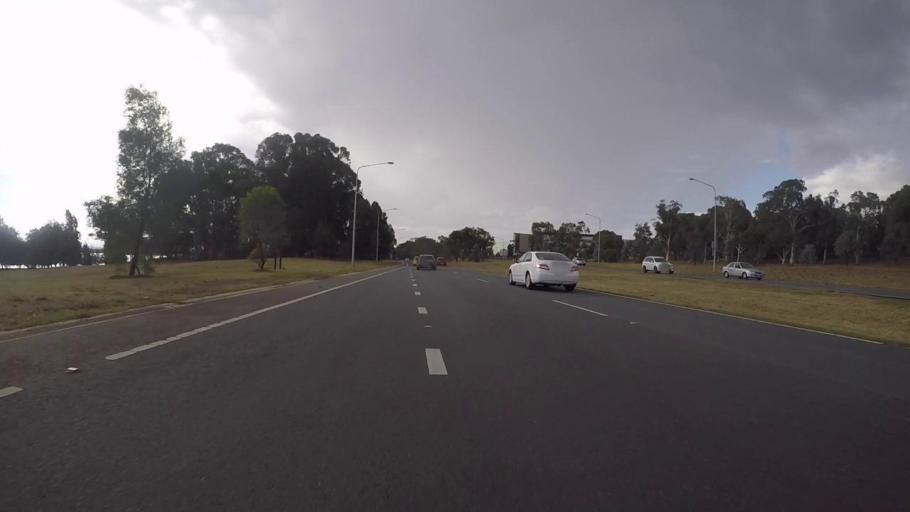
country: AU
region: Australian Capital Territory
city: Canberra
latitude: -35.2962
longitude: 149.1459
